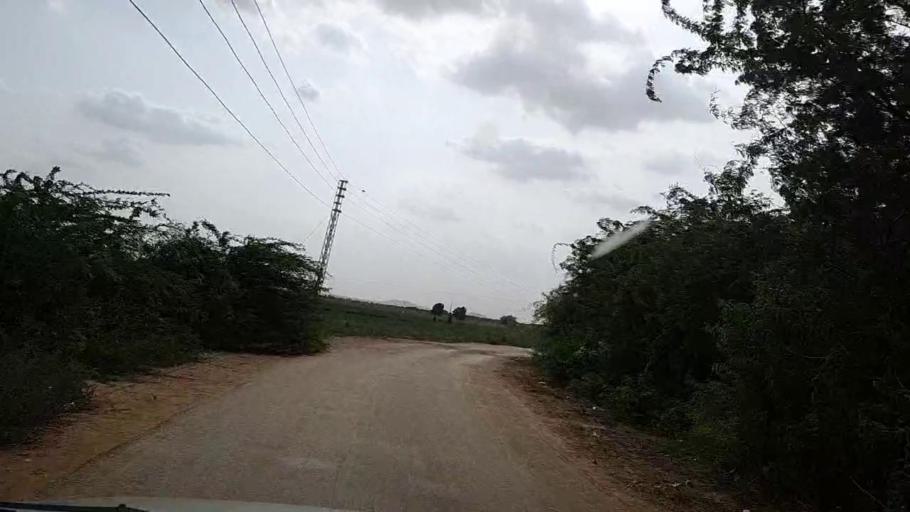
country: PK
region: Sindh
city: Kotri
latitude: 25.2564
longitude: 68.2554
